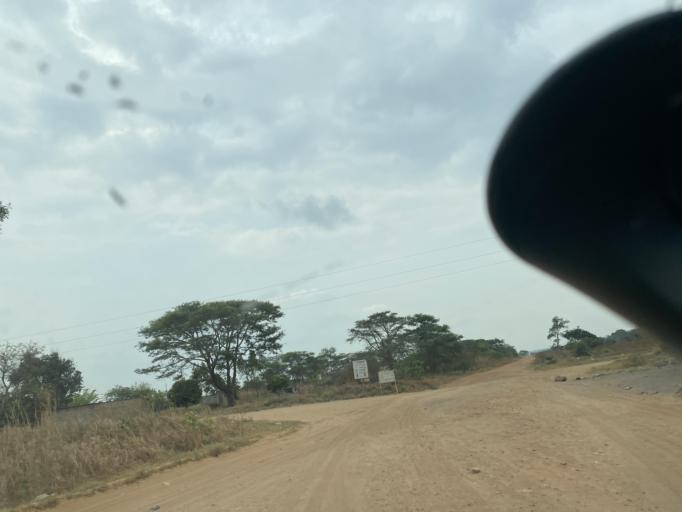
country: ZM
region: Lusaka
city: Lusaka
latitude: -15.2290
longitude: 28.3358
